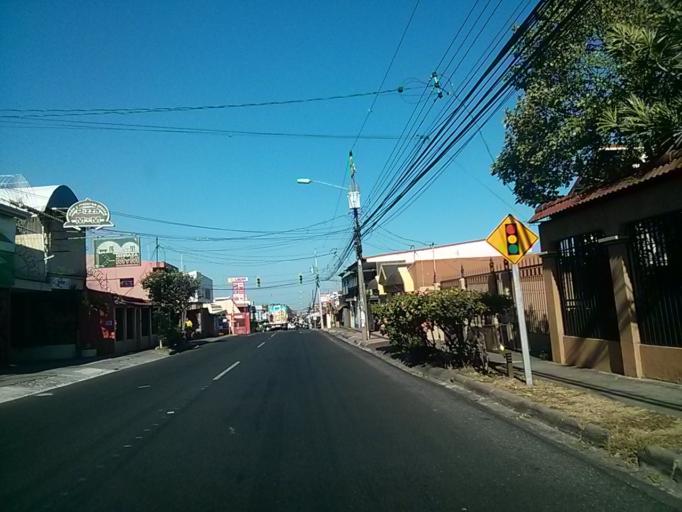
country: CR
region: Heredia
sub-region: Canton de Belen
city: San Antonio
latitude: 9.9801
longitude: -84.1817
